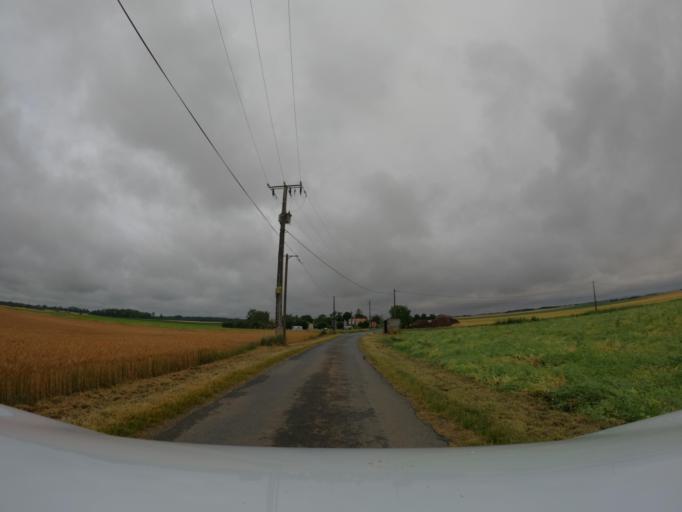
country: FR
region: Pays de la Loire
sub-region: Departement de la Vendee
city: Maillezais
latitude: 46.4030
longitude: -0.7218
